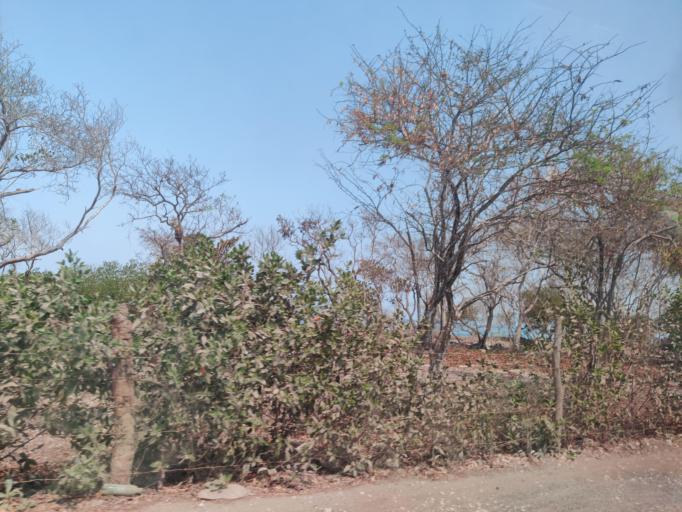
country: CO
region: Bolivar
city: Turbana
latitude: 10.1839
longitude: -75.6434
